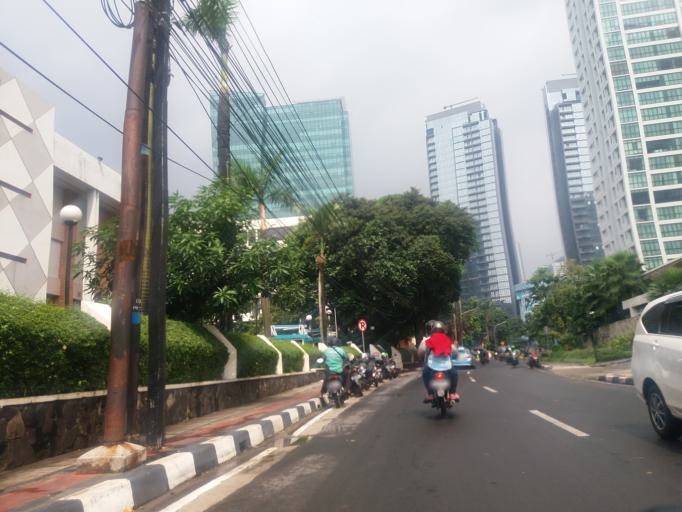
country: ID
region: Jakarta Raya
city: Jakarta
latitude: -6.2154
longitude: 106.8296
